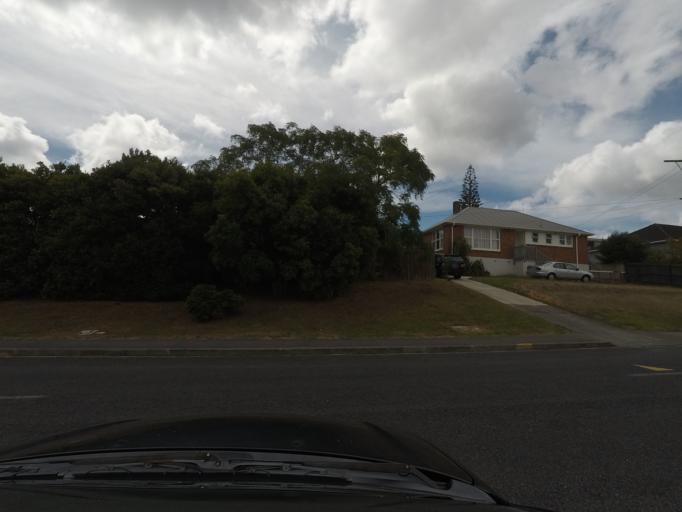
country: NZ
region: Auckland
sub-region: Auckland
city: Auckland
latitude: -36.8969
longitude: 174.7298
